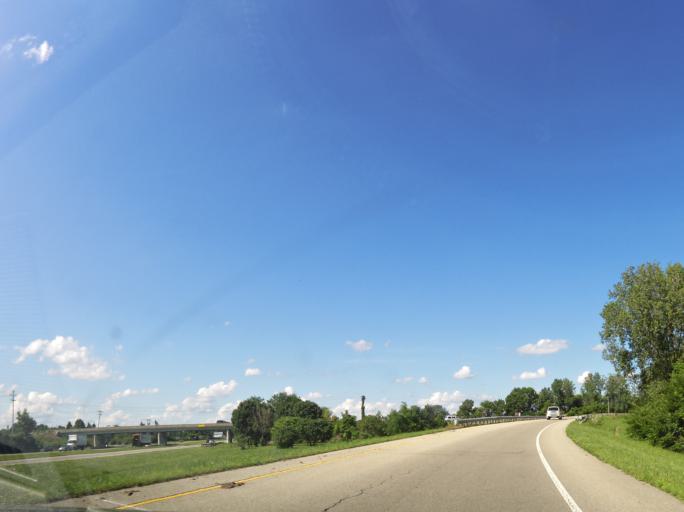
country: US
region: Ohio
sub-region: Greene County
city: Wright-Patterson AFB
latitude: 39.8420
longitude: -84.0590
